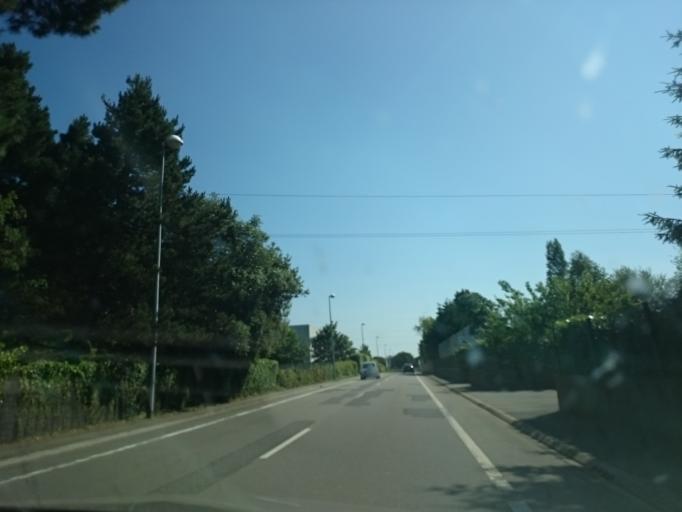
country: FR
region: Pays de la Loire
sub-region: Departement de la Loire-Atlantique
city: La Montagne
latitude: 47.1789
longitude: -1.6781
